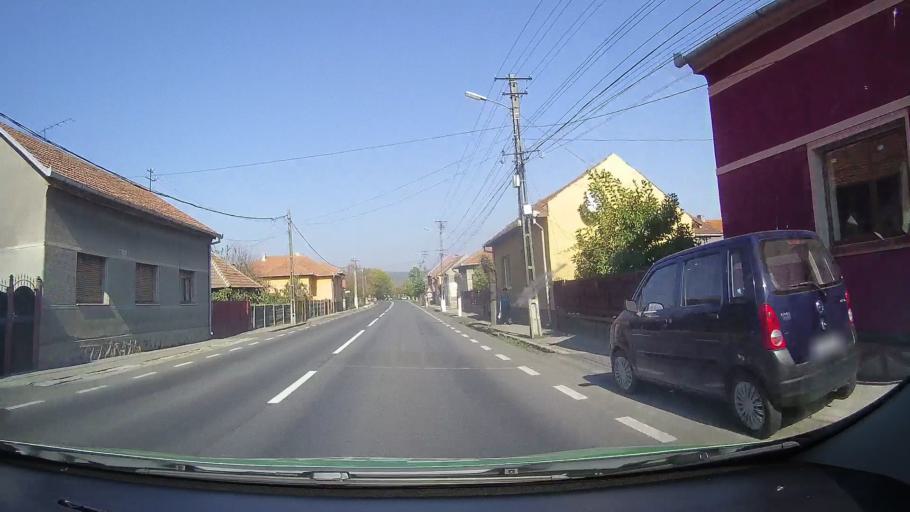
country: RO
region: Hunedoara
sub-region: Comuna Ilia
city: Ilia
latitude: 45.9378
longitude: 22.6506
